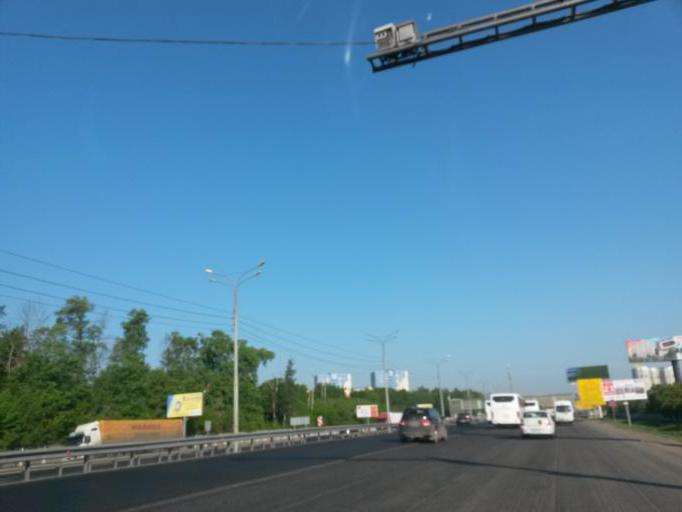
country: RU
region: Moskovskaya
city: Razvilka
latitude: 55.5867
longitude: 37.7379
